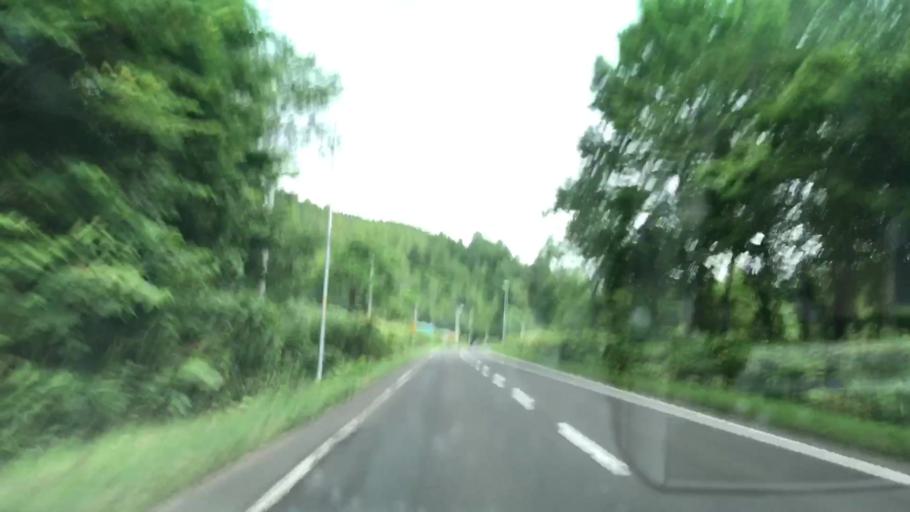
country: JP
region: Hokkaido
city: Niseko Town
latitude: 42.8218
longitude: 141.0027
